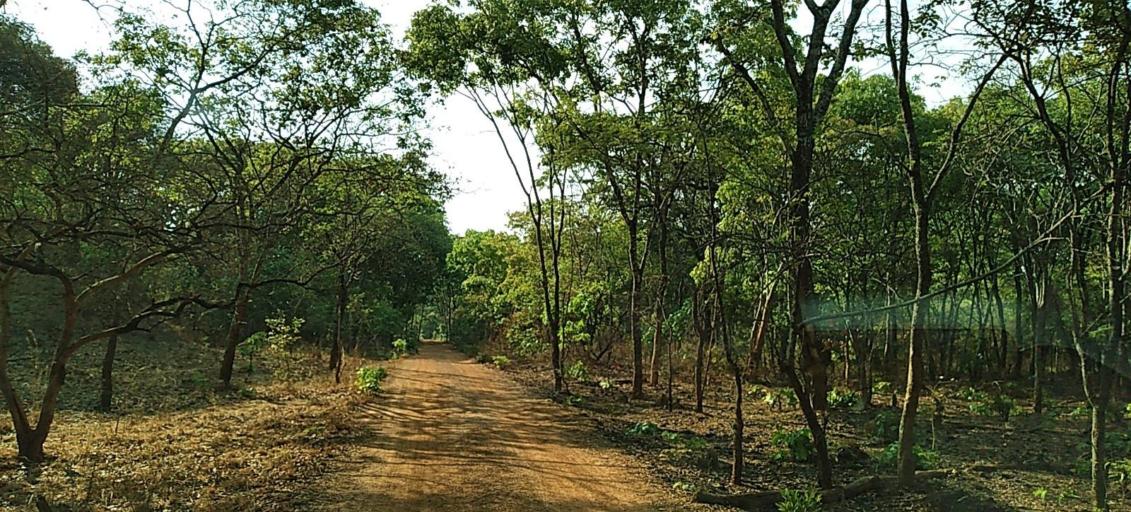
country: ZM
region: Copperbelt
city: Kalulushi
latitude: -12.9991
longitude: 27.7094
